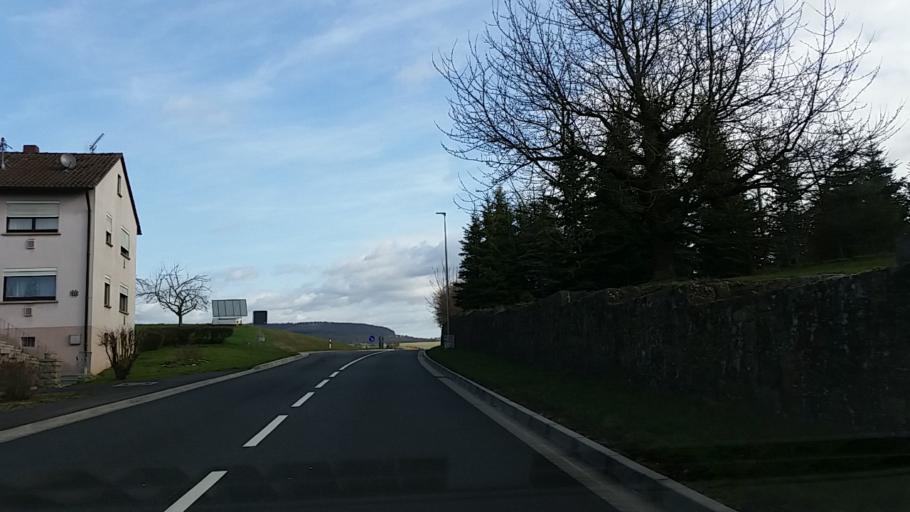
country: DE
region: Bavaria
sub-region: Regierungsbezirk Unterfranken
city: Karsbach
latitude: 50.0689
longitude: 9.7923
